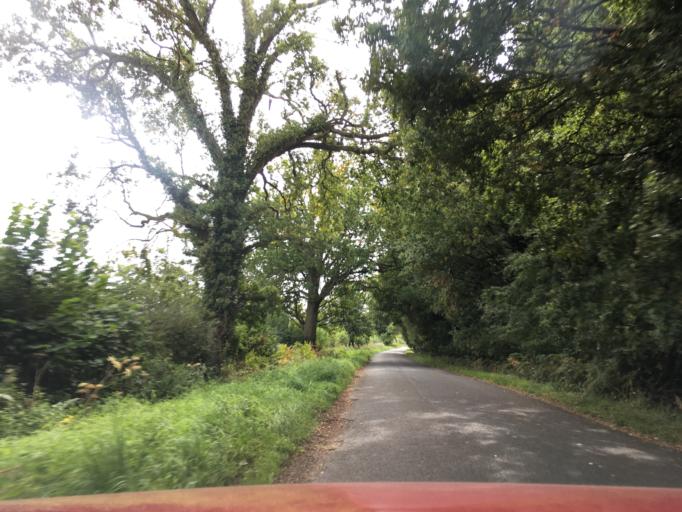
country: GB
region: England
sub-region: South Gloucestershire
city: Charfield
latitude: 51.6513
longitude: -2.4219
